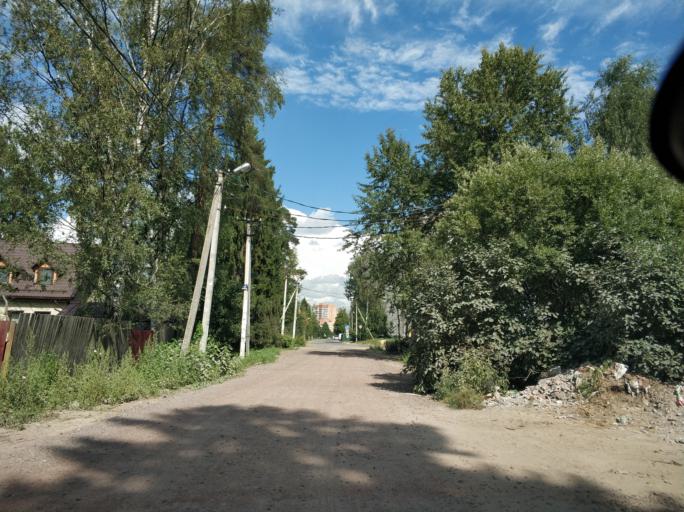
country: RU
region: Leningrad
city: Vsevolozhsk
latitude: 60.0219
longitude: 30.6193
